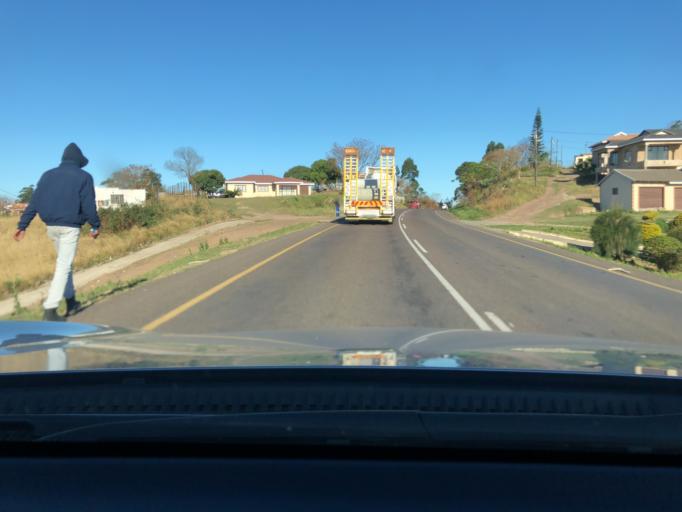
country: ZA
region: KwaZulu-Natal
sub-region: eThekwini Metropolitan Municipality
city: Umkomaas
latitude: -29.9963
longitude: 30.7963
